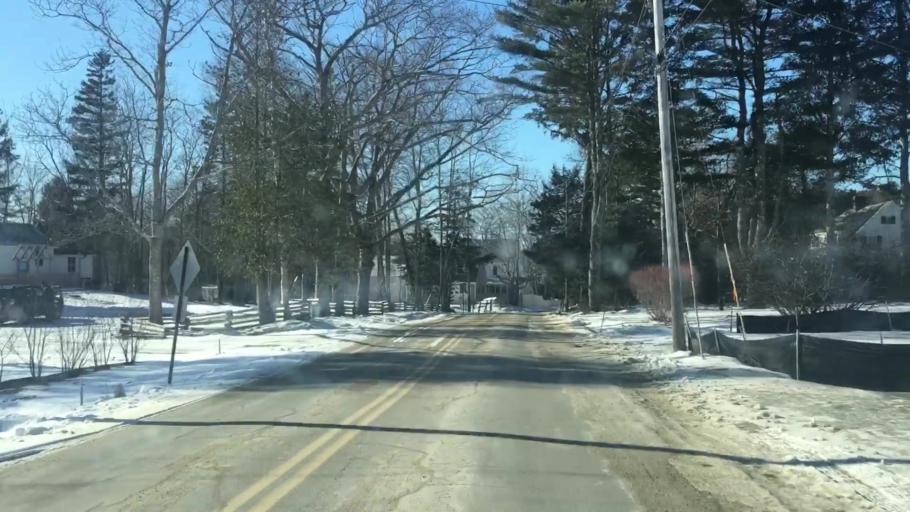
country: US
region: Maine
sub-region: Hancock County
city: Castine
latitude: 44.3415
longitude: -68.7365
